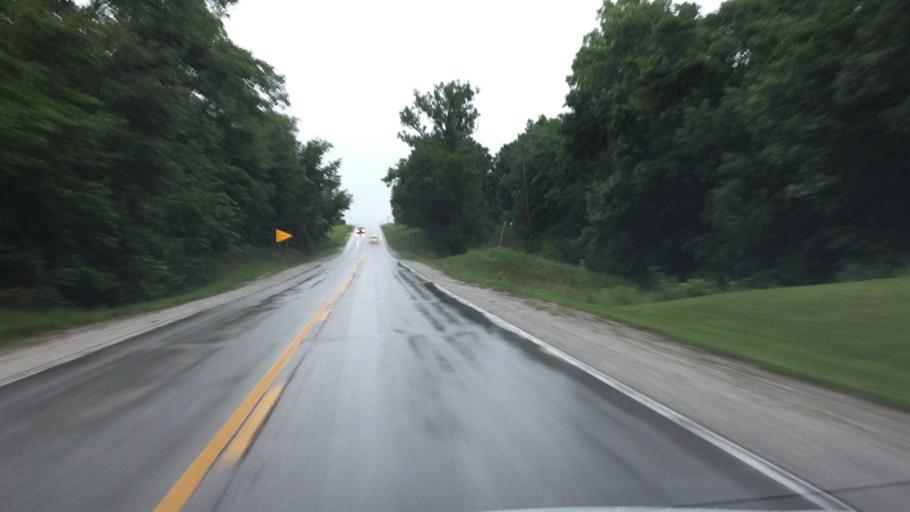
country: US
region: Illinois
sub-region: Hancock County
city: Carthage
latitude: 40.4392
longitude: -91.1400
